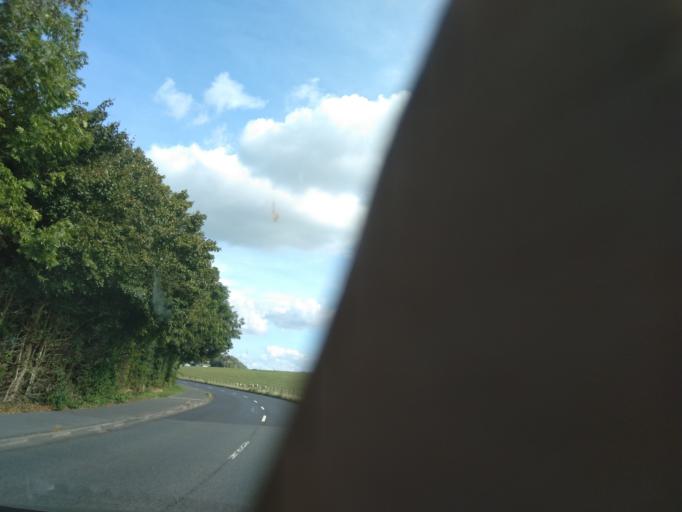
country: DE
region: Lower Saxony
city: Leer
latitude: 53.2149
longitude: 7.4430
